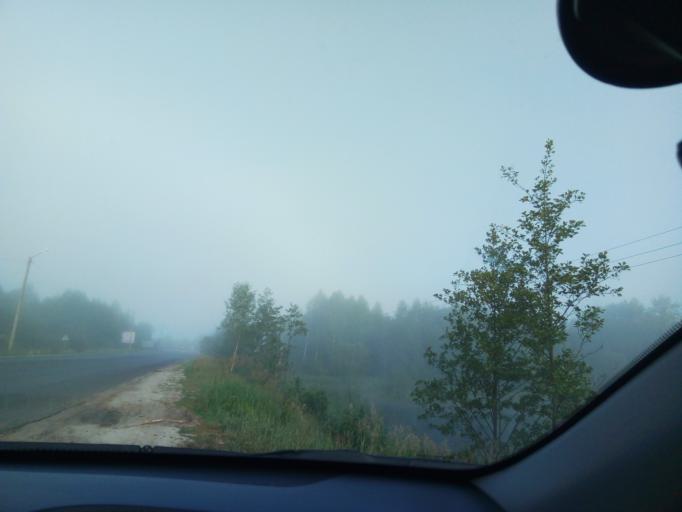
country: RU
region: Nizjnij Novgorod
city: Voznesenskoye
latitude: 54.8893
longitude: 42.7527
